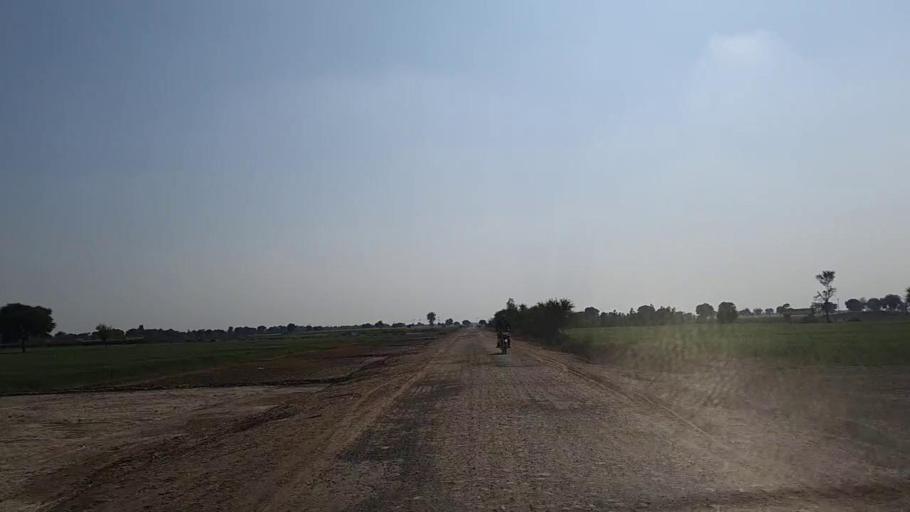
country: PK
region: Sindh
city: Jam Sahib
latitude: 26.2669
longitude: 68.5672
